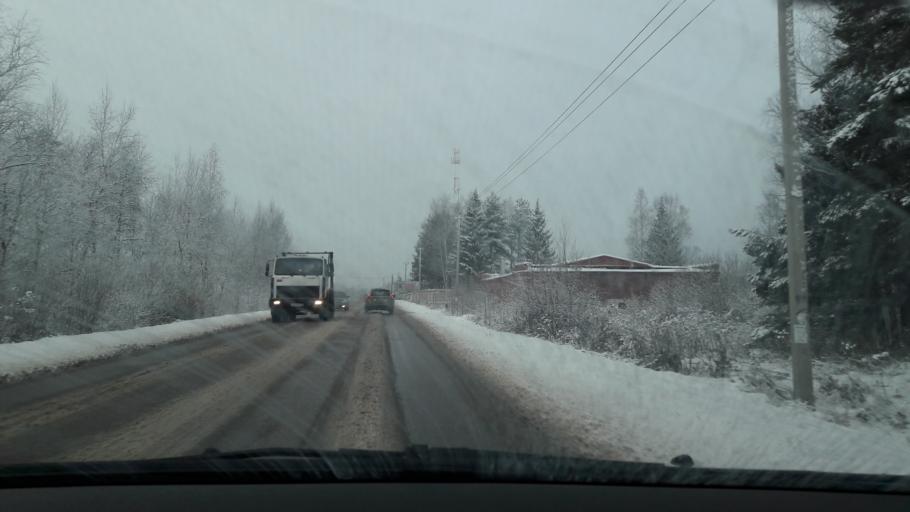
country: RU
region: Moskovskaya
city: Zvenigorod
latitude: 55.6413
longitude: 36.8400
